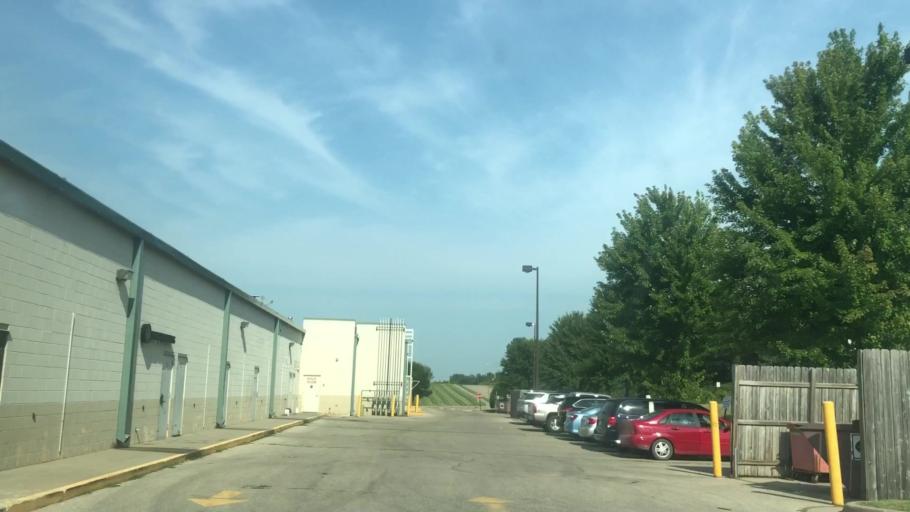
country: US
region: Iowa
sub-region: Marshall County
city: Marshalltown
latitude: 42.0107
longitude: -92.9118
